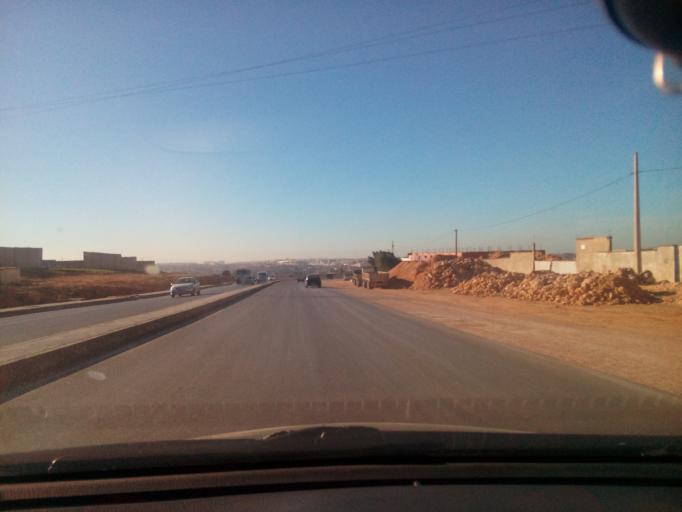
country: DZ
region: Mostaganem
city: Mostaganem
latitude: 35.9125
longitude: 0.1423
